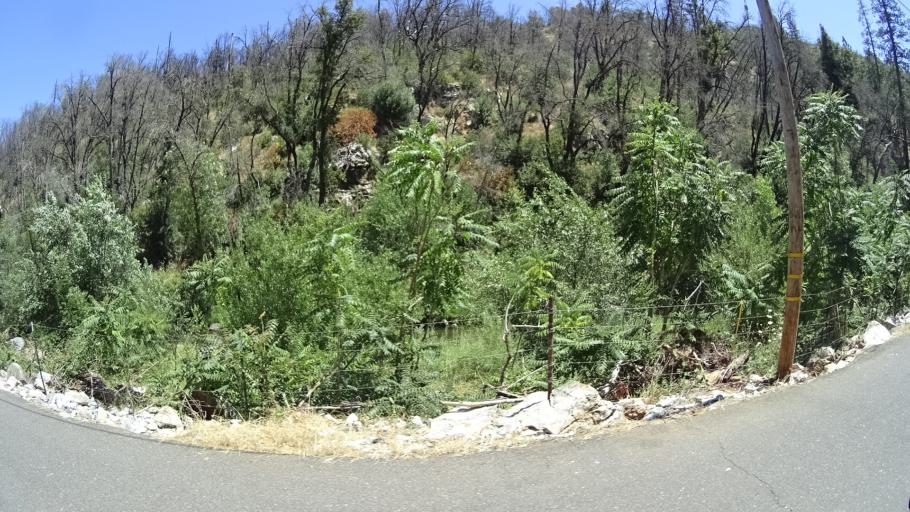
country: US
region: California
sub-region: Calaveras County
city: San Andreas
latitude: 38.2858
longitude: -120.6646
